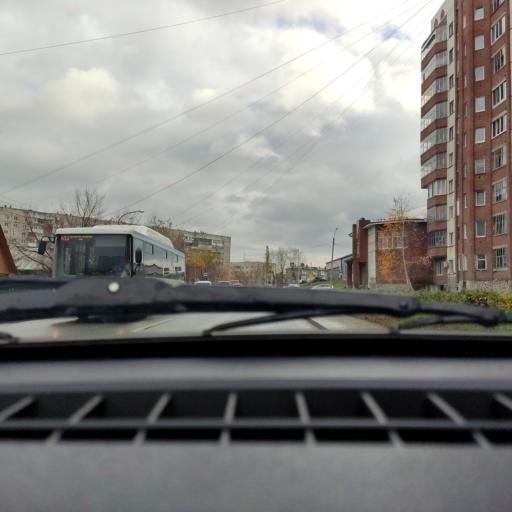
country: RU
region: Bashkortostan
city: Ufa
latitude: 54.8199
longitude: 56.1211
